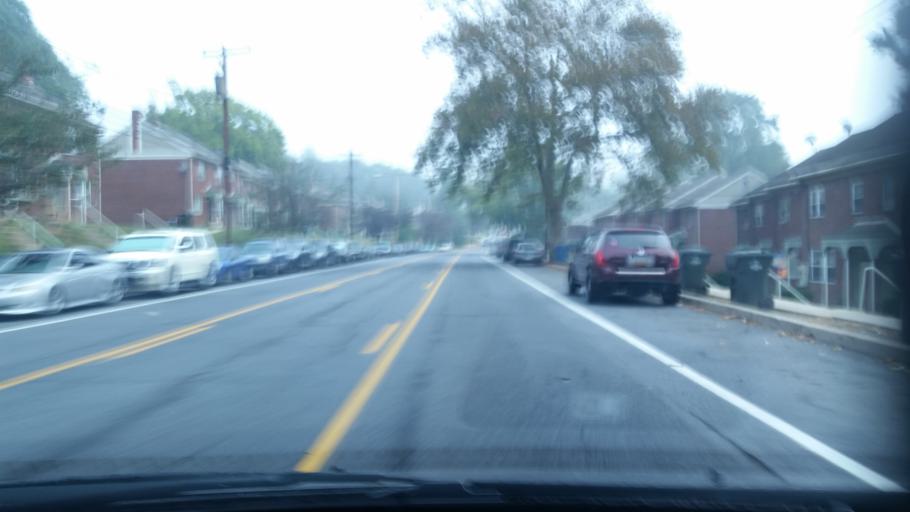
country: US
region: Pennsylvania
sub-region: Lancaster County
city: Lancaster
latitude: 40.0336
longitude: -76.2876
